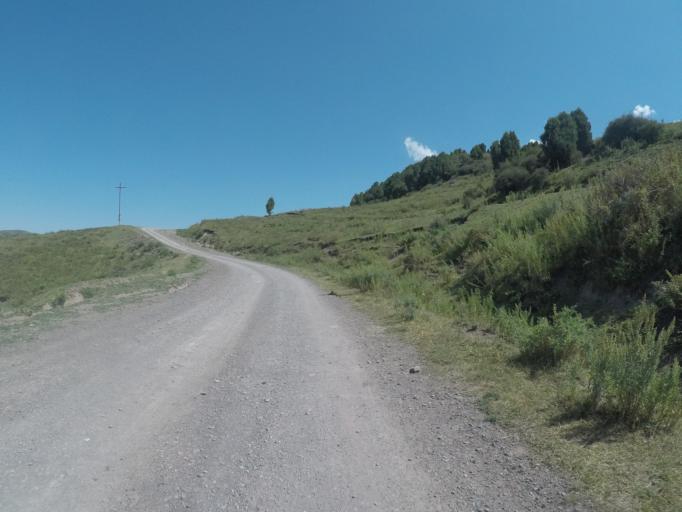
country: KG
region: Chuy
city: Bishkek
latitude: 42.6510
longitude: 74.5263
